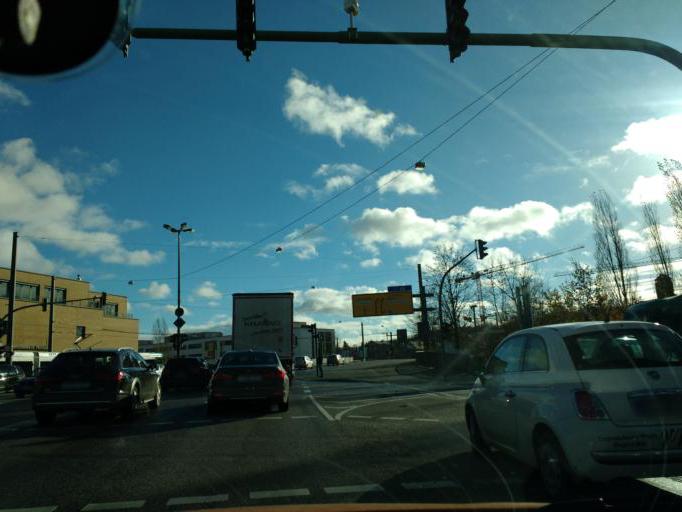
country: DE
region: Brandenburg
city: Potsdam
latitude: 52.3927
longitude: 13.0629
